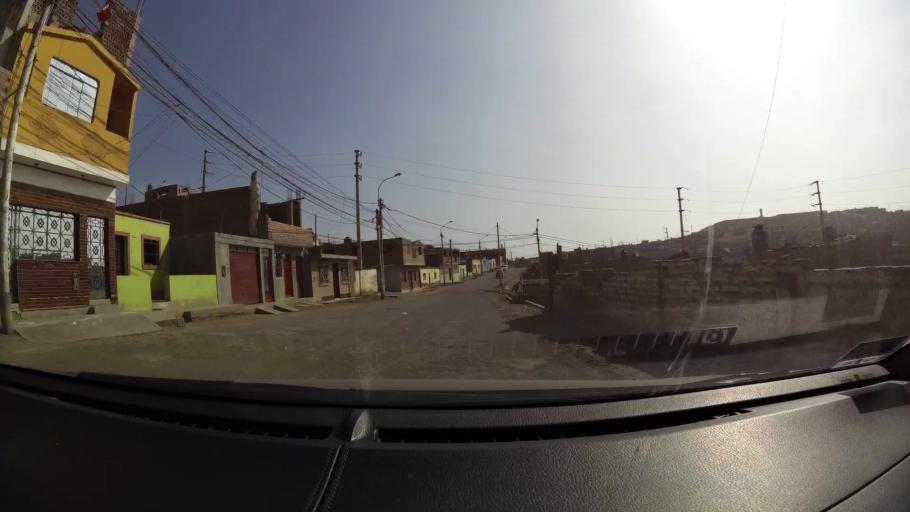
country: PE
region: Lima
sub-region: Huaura
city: Huacho
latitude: -11.1278
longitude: -77.6141
